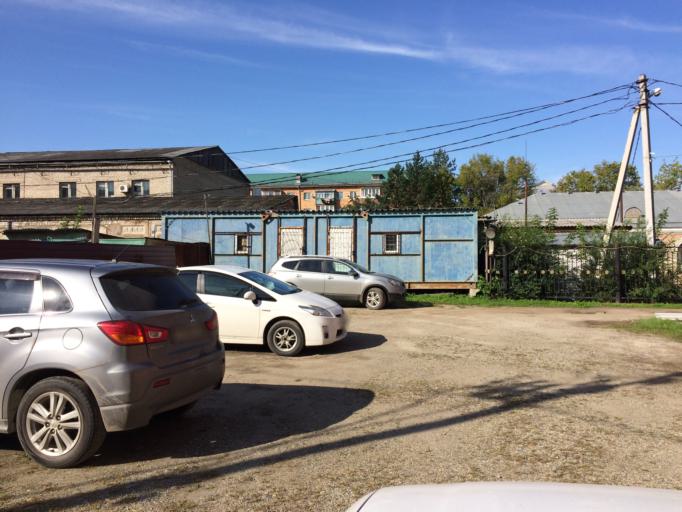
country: RU
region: Primorskiy
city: Dal'nerechensk
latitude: 45.9336
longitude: 133.7362
